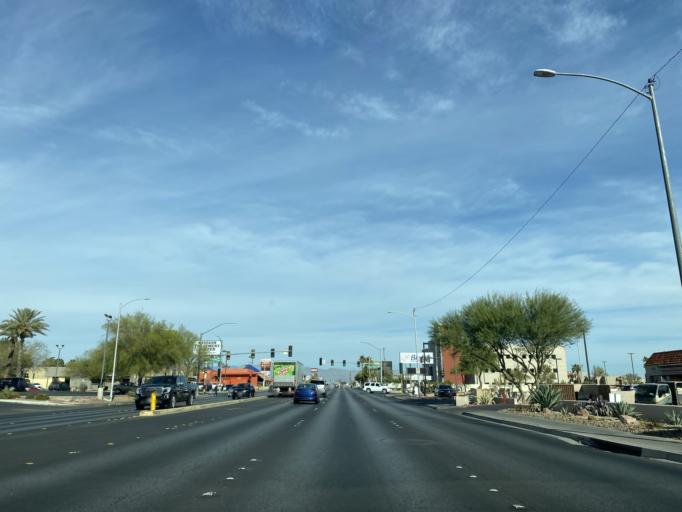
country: US
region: Nevada
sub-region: Clark County
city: Winchester
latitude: 36.1360
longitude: -115.1368
